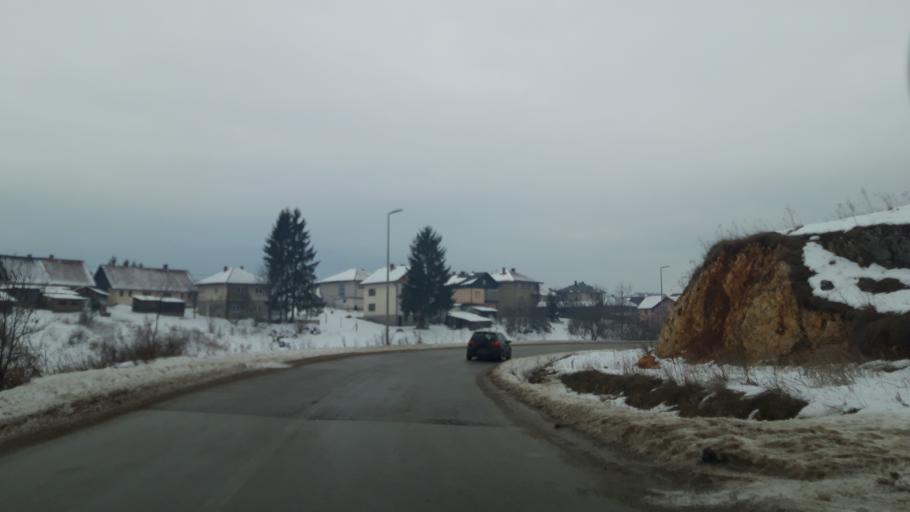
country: BA
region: Republika Srpska
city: Sokolac
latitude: 43.9353
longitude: 18.8024
